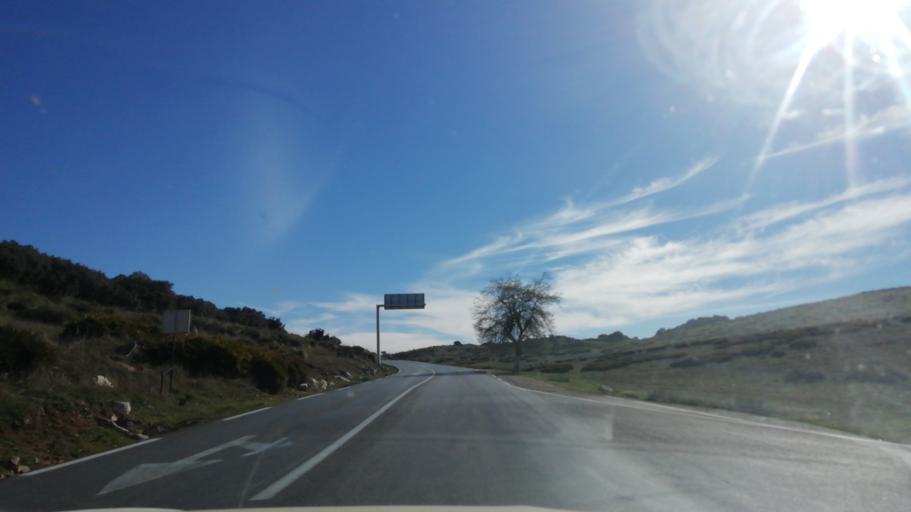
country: DZ
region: Tlemcen
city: Mansoura
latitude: 34.8304
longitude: -1.3710
